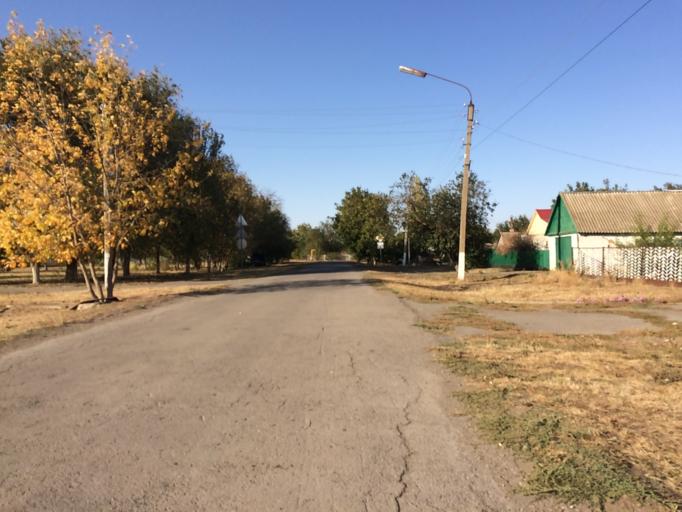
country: RU
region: Rostov
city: Tselina
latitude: 46.5180
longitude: 41.1840
